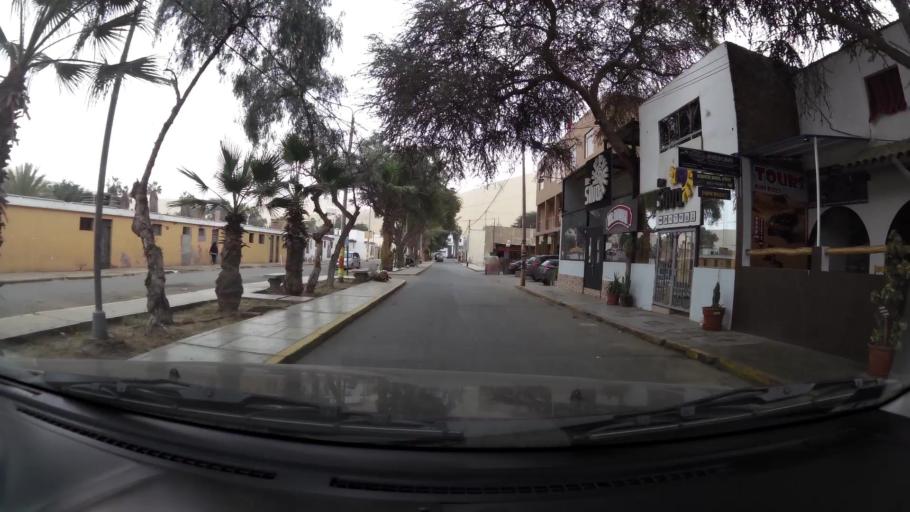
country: PE
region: Ica
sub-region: Provincia de Ica
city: Ica
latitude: -14.0867
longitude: -75.7624
